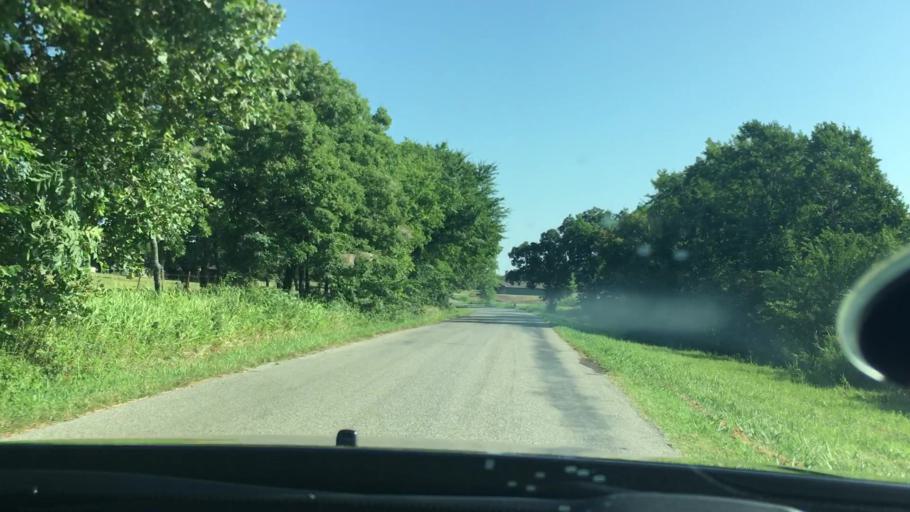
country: US
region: Oklahoma
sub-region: Pontotoc County
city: Byng
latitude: 34.8133
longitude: -96.6261
